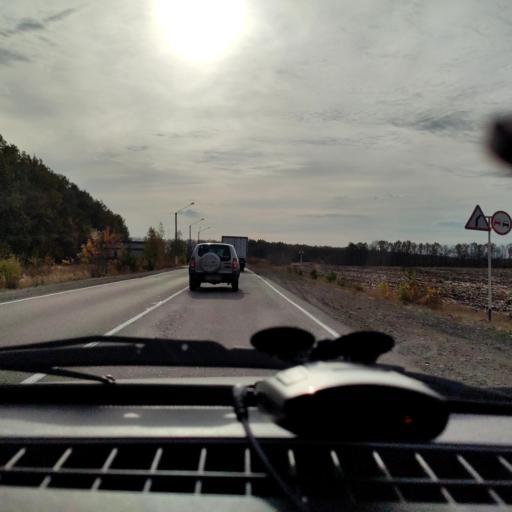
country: RU
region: Voronezj
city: Shilovo
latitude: 51.4307
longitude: 39.0061
